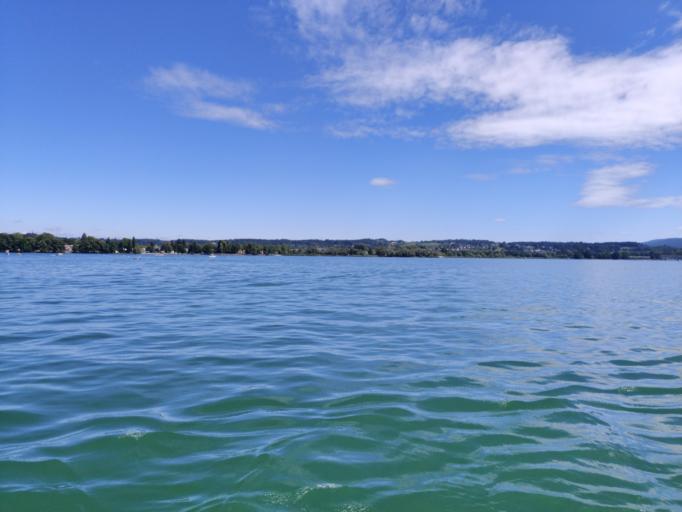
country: DE
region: Bavaria
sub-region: Swabia
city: Lindau
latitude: 47.5402
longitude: 9.6944
